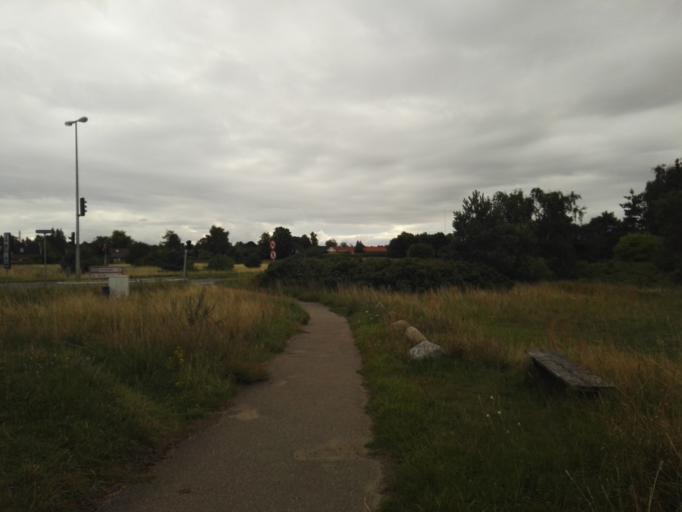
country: DK
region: Zealand
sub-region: Odsherred Kommune
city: Nykobing Sjaelland
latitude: 55.9335
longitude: 11.6674
